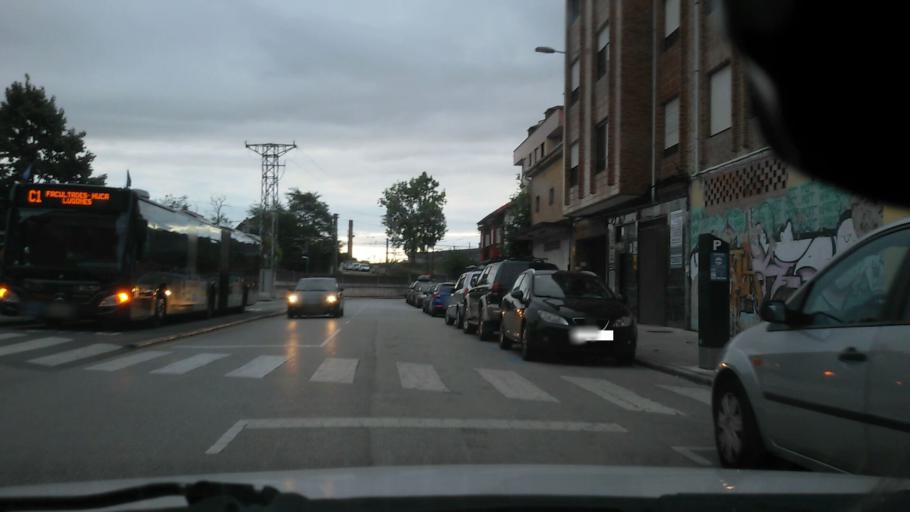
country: ES
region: Asturias
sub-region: Province of Asturias
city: Lugones
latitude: 43.4039
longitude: -5.8113
